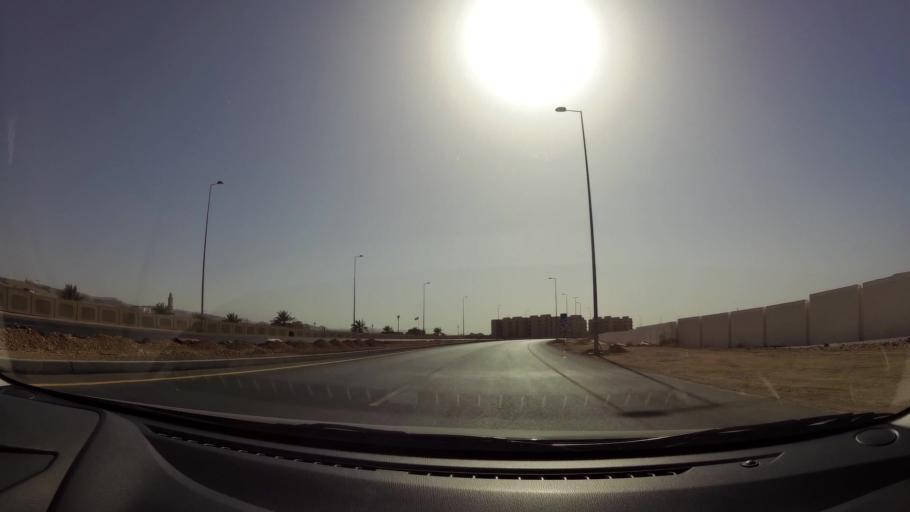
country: OM
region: Muhafazat Masqat
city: Bawshar
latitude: 23.5737
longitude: 58.2814
